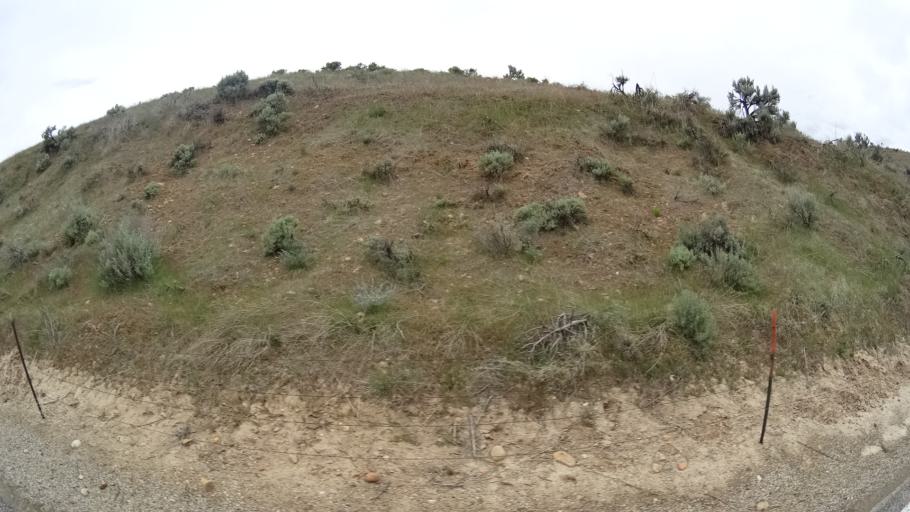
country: US
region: Idaho
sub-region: Ada County
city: Boise
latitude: 43.4869
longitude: -116.0166
